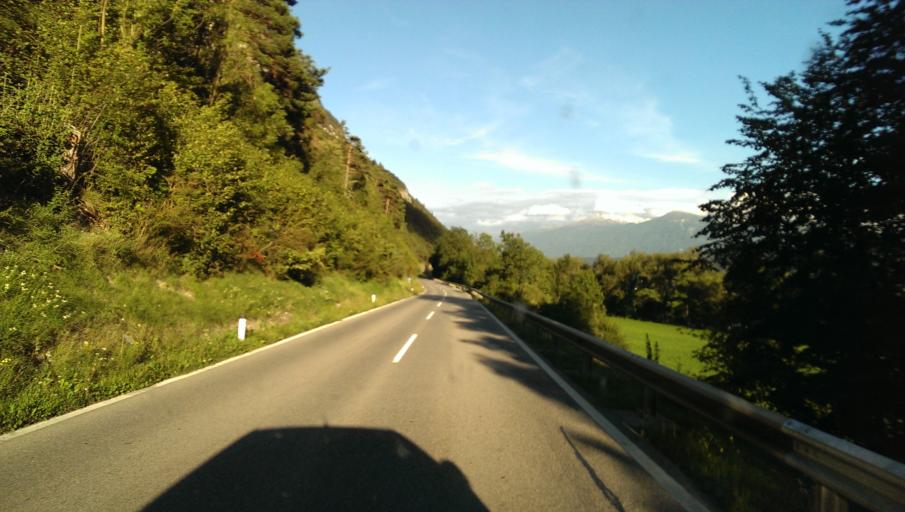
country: AT
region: Tyrol
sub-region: Politischer Bezirk Innsbruck Land
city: Kematen in Tirol
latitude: 47.2671
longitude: 11.2735
